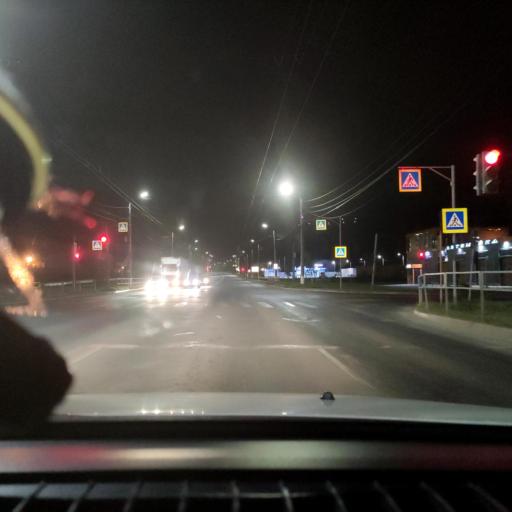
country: RU
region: Samara
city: Novokuybyshevsk
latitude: 53.0973
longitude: 49.9399
